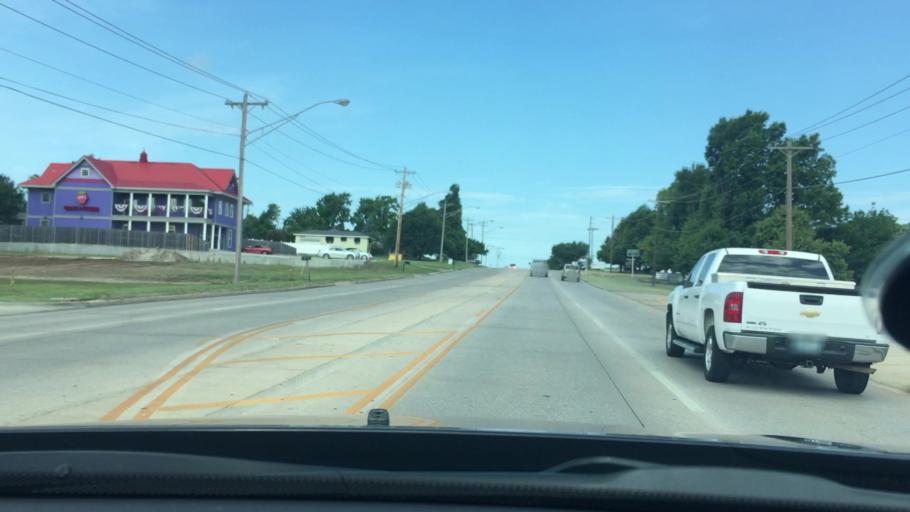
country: US
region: Oklahoma
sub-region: Pontotoc County
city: Ada
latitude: 34.7817
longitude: -96.6569
